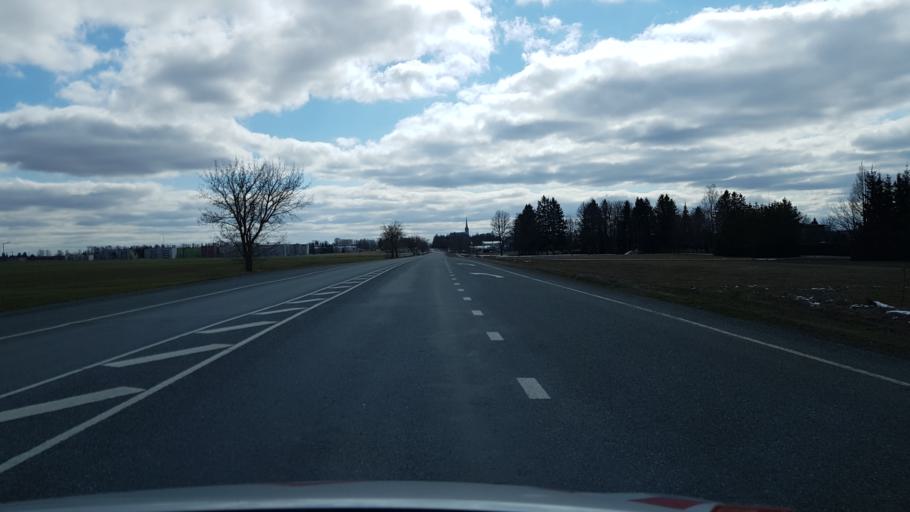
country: EE
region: Laeaene-Virumaa
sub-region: Kadrina vald
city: Kadrina
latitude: 59.3517
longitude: 26.1209
